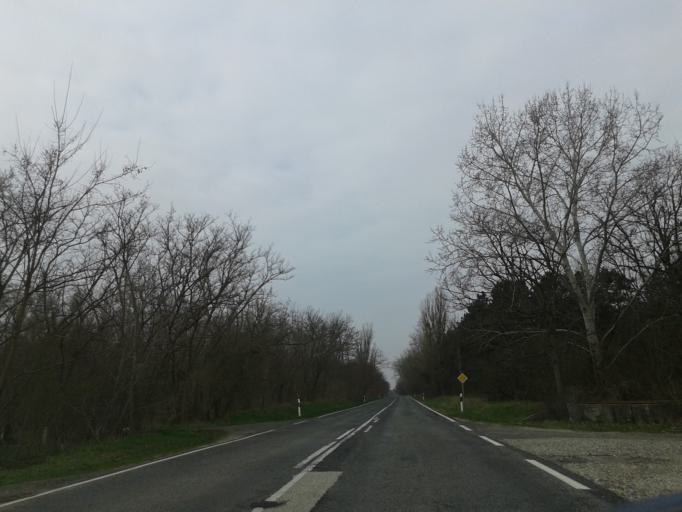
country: HU
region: Gyor-Moson-Sopron
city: Bony
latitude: 47.7334
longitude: 17.8854
